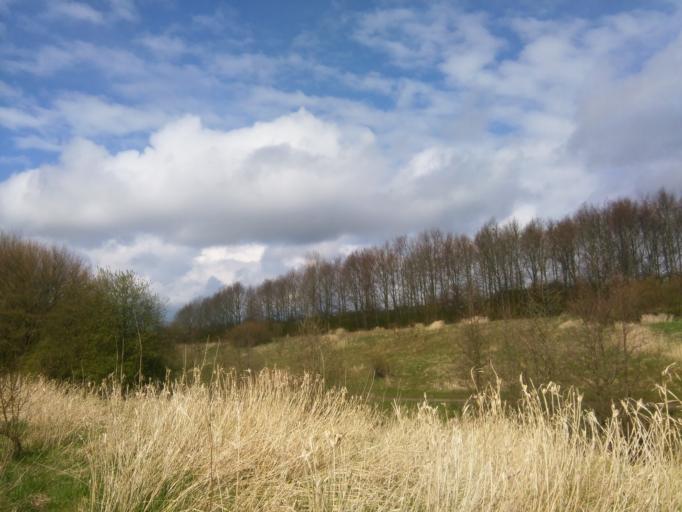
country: DK
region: Central Jutland
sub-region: Arhus Kommune
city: Stavtrup
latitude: 56.1724
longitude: 10.1043
